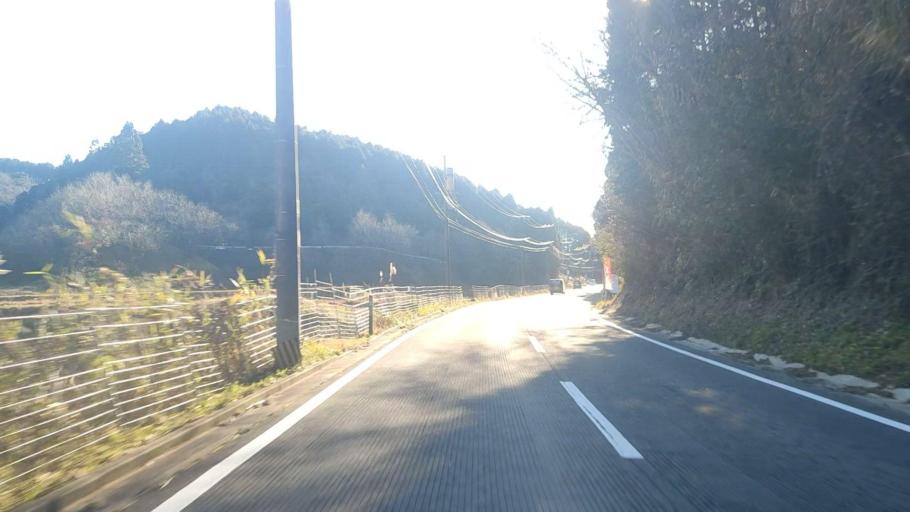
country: JP
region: Saga Prefecture
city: Kanzakimachi-kanzaki
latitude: 33.4158
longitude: 130.2781
